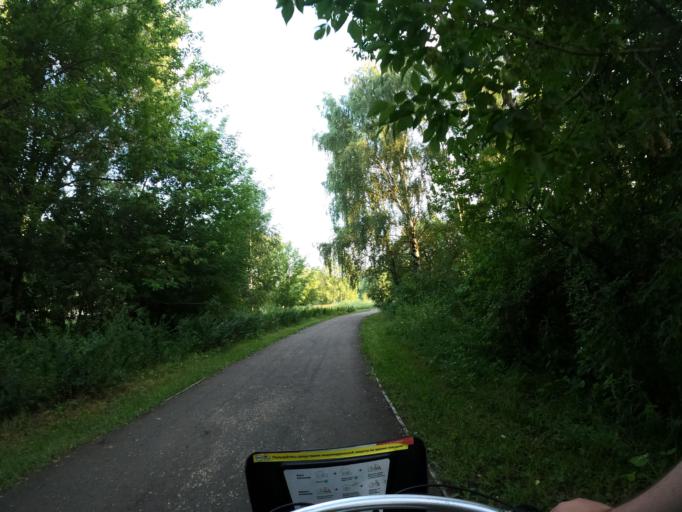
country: RU
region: Moscow
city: Strogino
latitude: 55.8192
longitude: 37.4109
